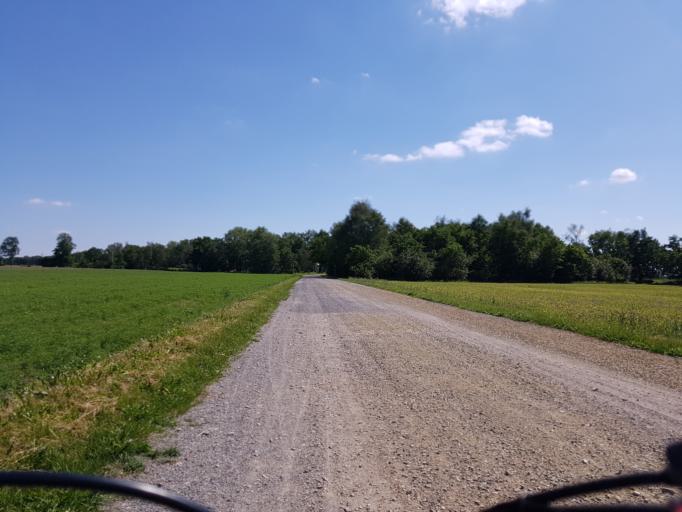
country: DE
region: Brandenburg
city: Elsterwerda
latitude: 51.4405
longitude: 13.5318
